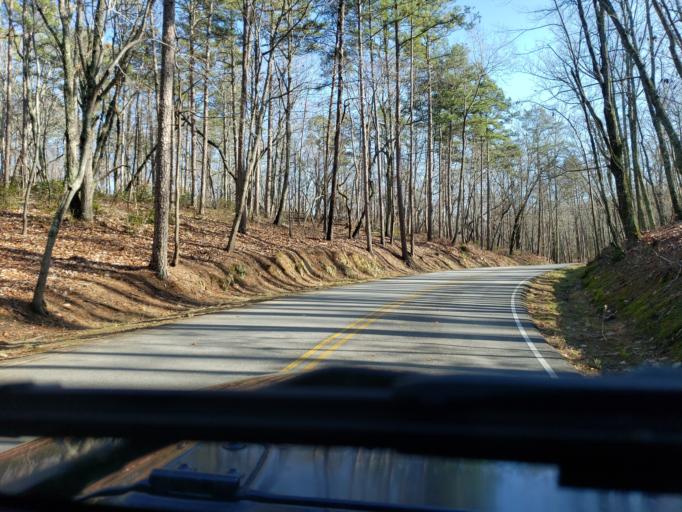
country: US
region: North Carolina
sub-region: Cleveland County
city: White Plains
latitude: 35.1500
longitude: -81.3909
